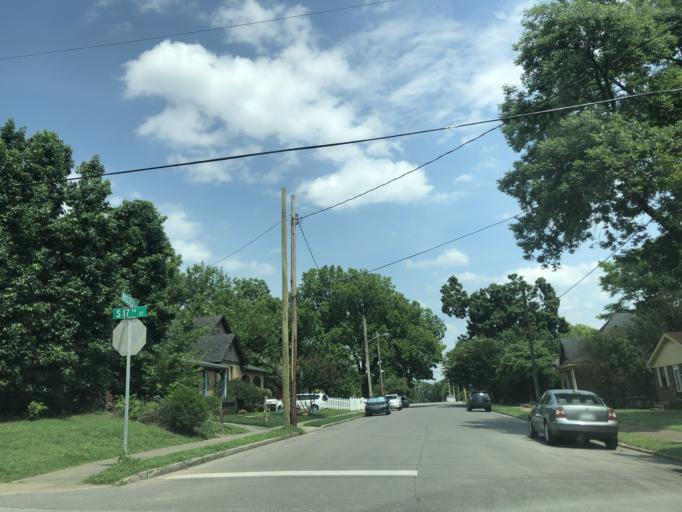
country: US
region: Tennessee
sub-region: Davidson County
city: Nashville
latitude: 36.1742
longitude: -86.7398
